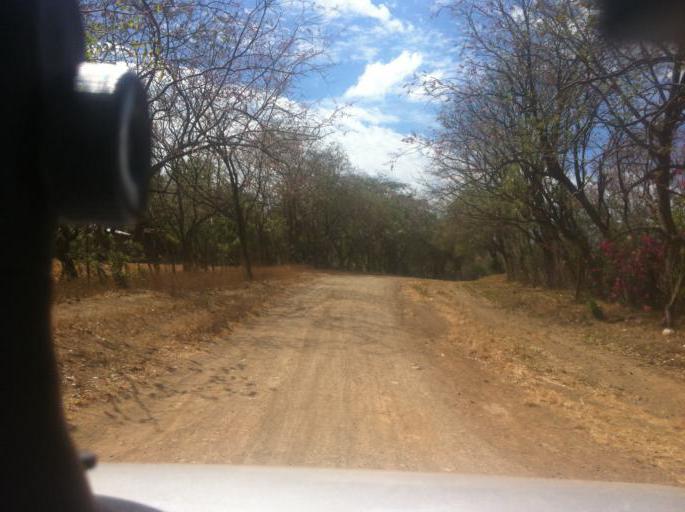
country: NI
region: Granada
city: Nandaime
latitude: 11.6309
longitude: -86.0170
